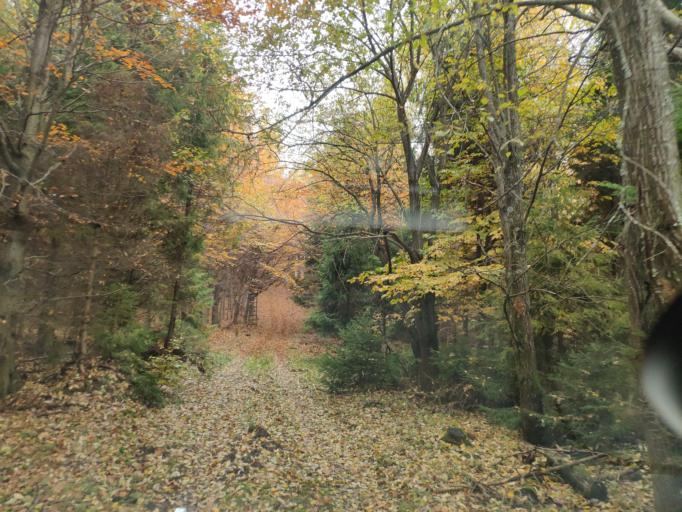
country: SK
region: Kosicky
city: Medzev
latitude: 48.7439
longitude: 20.9904
